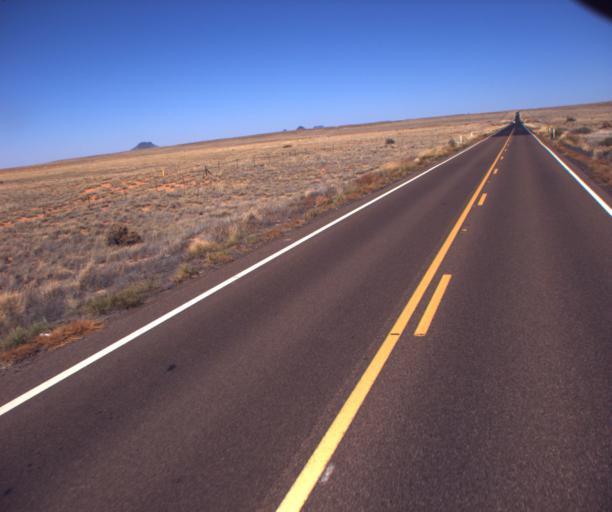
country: US
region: Arizona
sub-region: Navajo County
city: Dilkon
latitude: 35.2599
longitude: -110.4296
